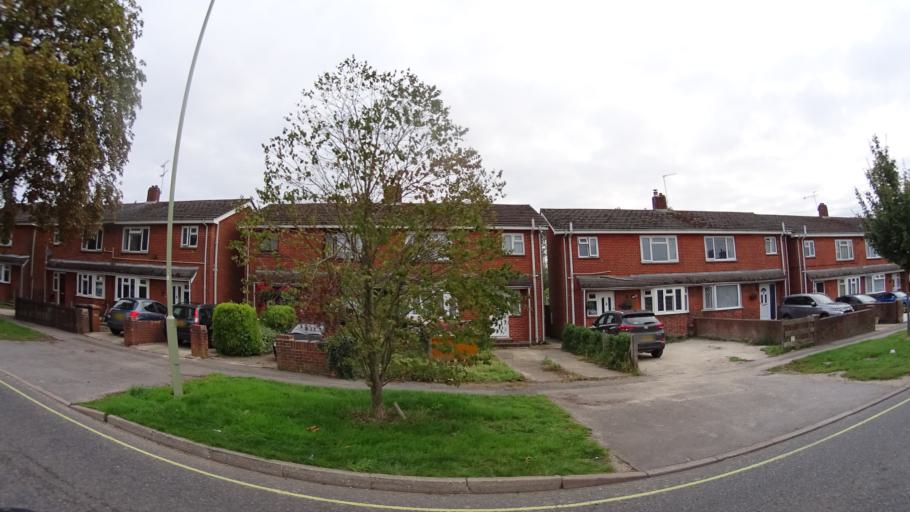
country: GB
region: England
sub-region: Hampshire
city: Romsey
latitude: 50.9928
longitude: -1.4951
